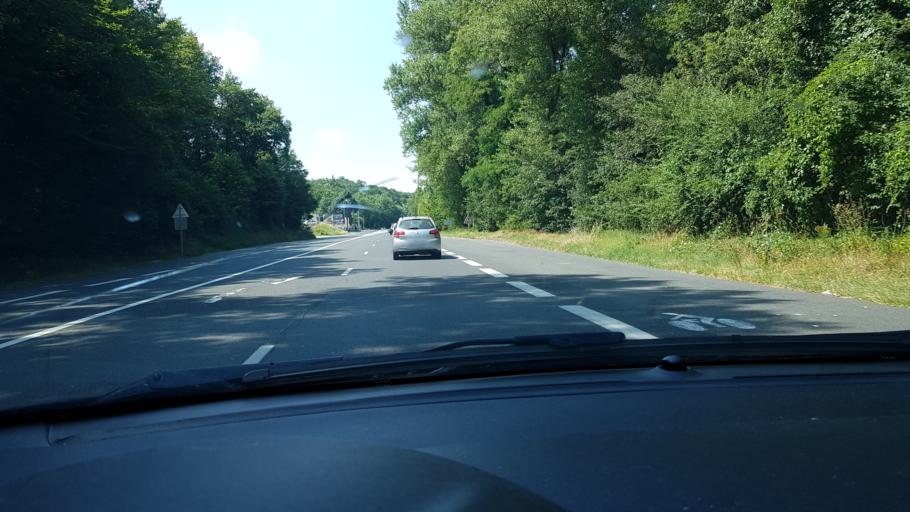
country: FR
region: Rhone-Alpes
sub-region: Departement du Rhone
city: Montagny
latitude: 45.6223
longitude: 4.7649
